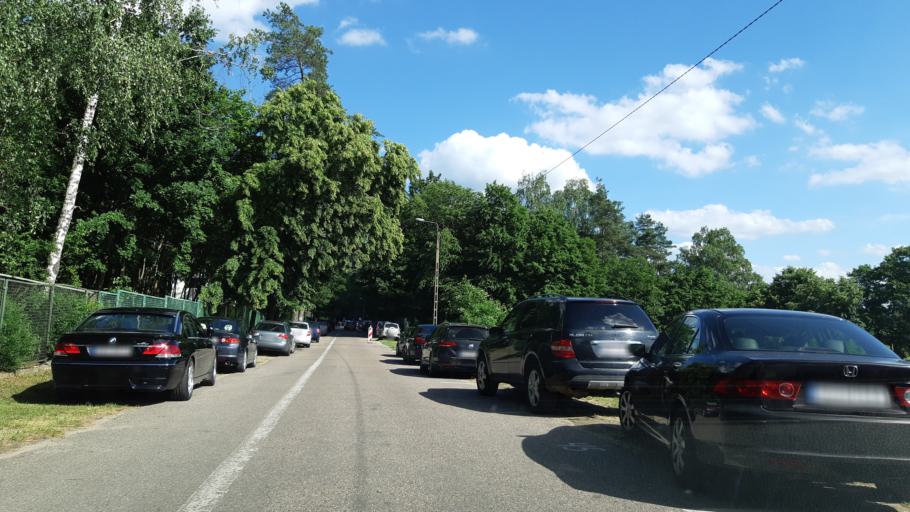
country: PL
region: Warmian-Masurian Voivodeship
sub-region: Powiat mragowski
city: Mragowo
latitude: 53.8749
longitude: 21.3186
